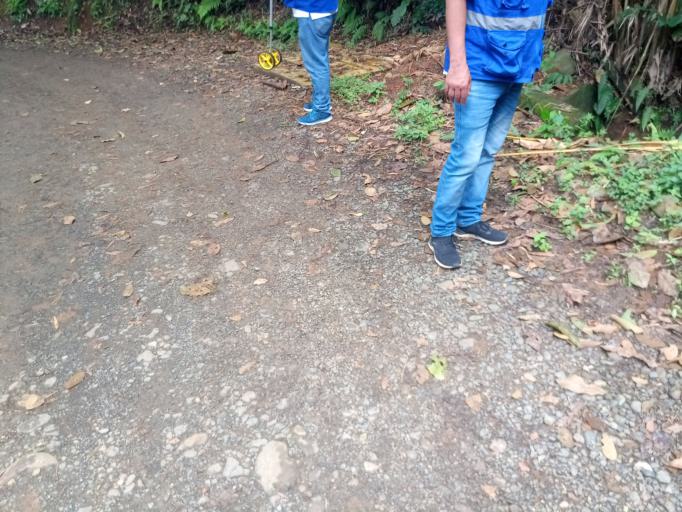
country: CO
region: Valle del Cauca
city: Cali
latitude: 3.5069
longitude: -76.5649
